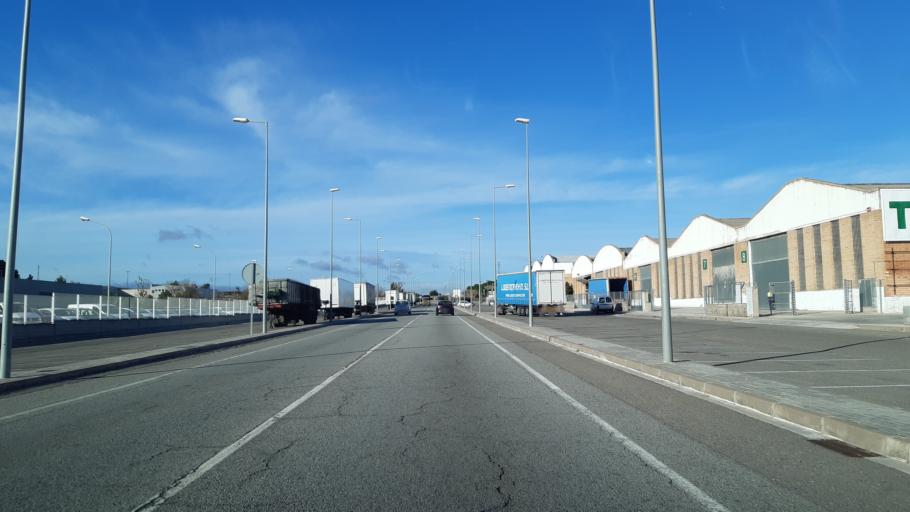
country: ES
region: Catalonia
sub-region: Provincia de Barcelona
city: Vilanova del Cami
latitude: 41.5774
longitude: 1.6540
